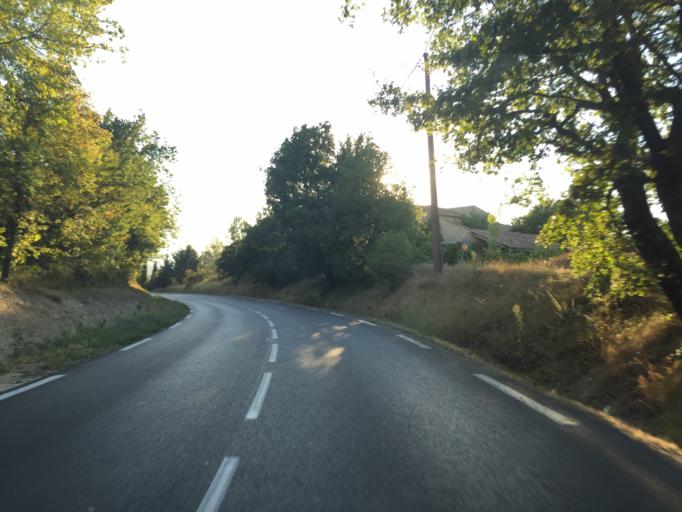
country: FR
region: Provence-Alpes-Cote d'Azur
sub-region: Departement des Alpes-de-Haute-Provence
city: Cereste
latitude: 43.8589
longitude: 5.5678
